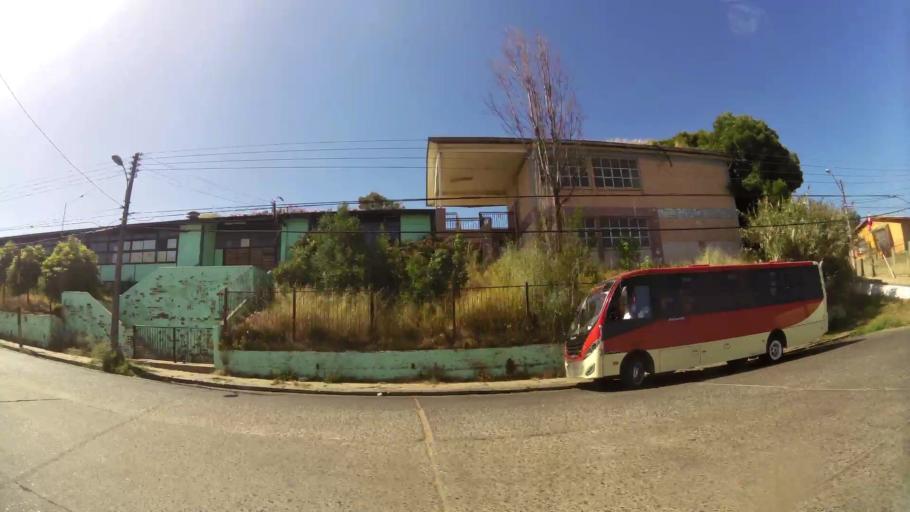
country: CL
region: Valparaiso
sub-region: Provincia de Valparaiso
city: Valparaiso
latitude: -33.0450
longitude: -71.6524
